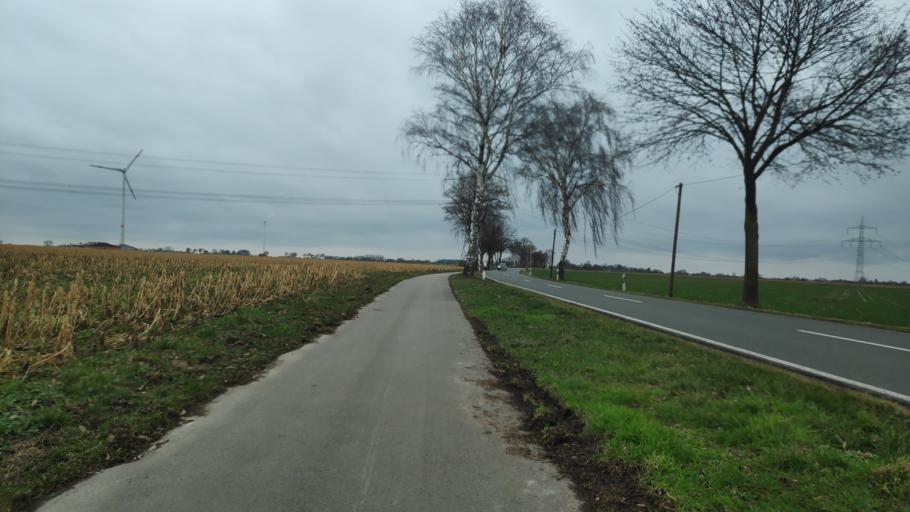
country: DE
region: North Rhine-Westphalia
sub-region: Regierungsbezirk Detmold
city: Hille
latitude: 52.3208
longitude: 8.8129
